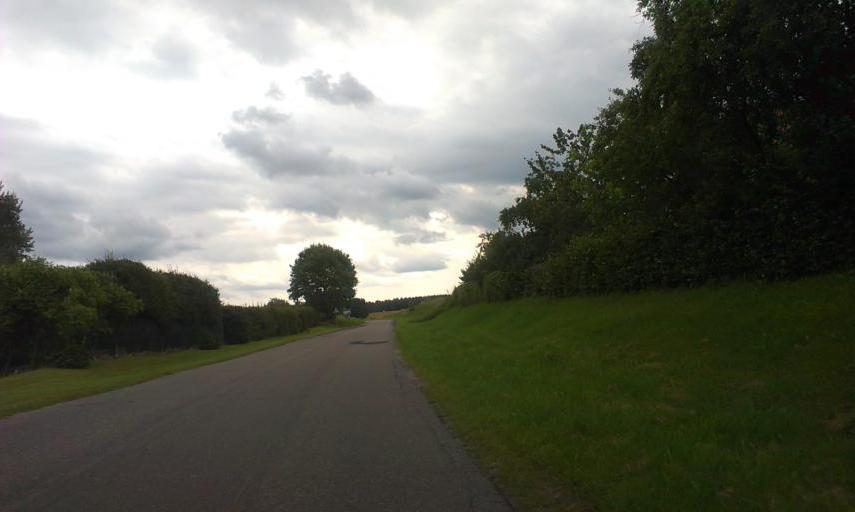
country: PL
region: West Pomeranian Voivodeship
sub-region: Powiat bialogardzki
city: Tychowo
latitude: 53.9704
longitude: 16.2101
